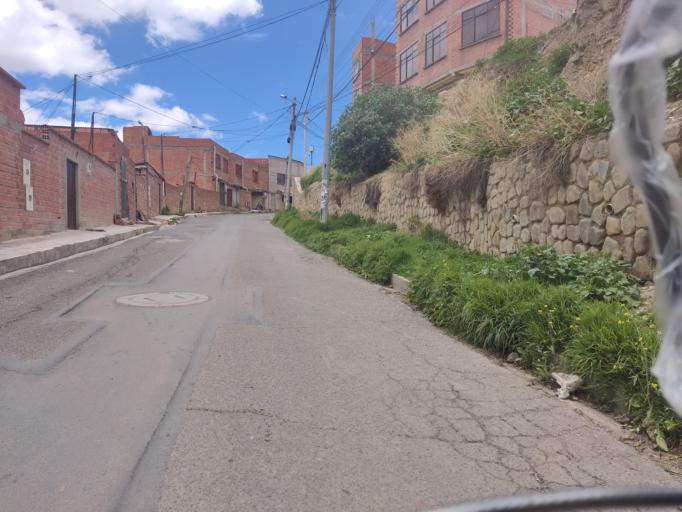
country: BO
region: La Paz
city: La Paz
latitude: -16.4900
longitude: -68.1483
